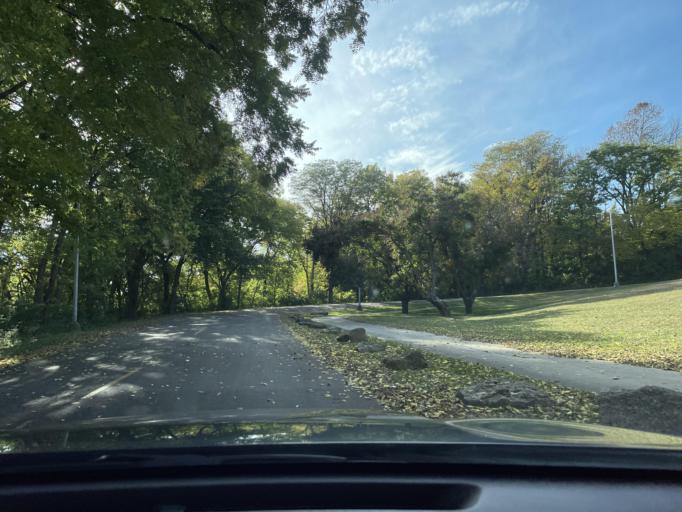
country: US
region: Kansas
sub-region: Doniphan County
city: Elwood
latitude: 39.7197
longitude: -94.8504
